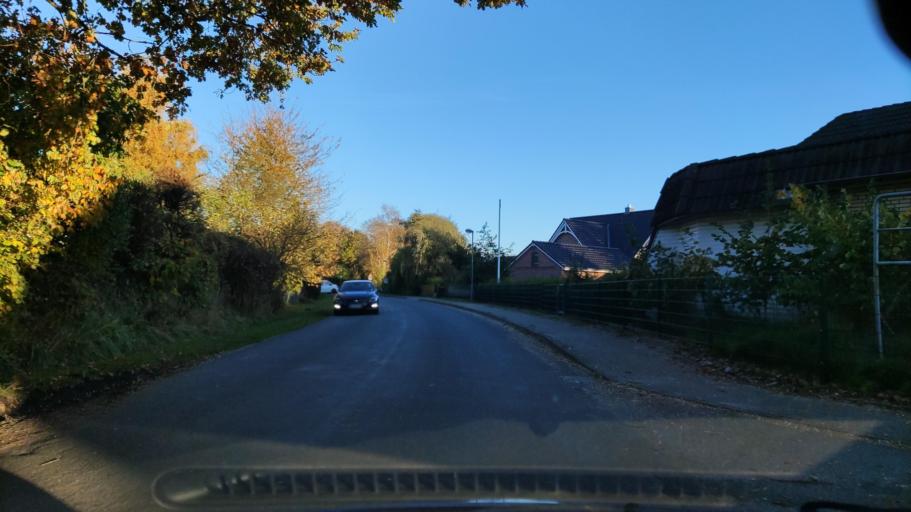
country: DE
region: Schleswig-Holstein
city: Basthorst
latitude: 53.5783
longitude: 10.4689
